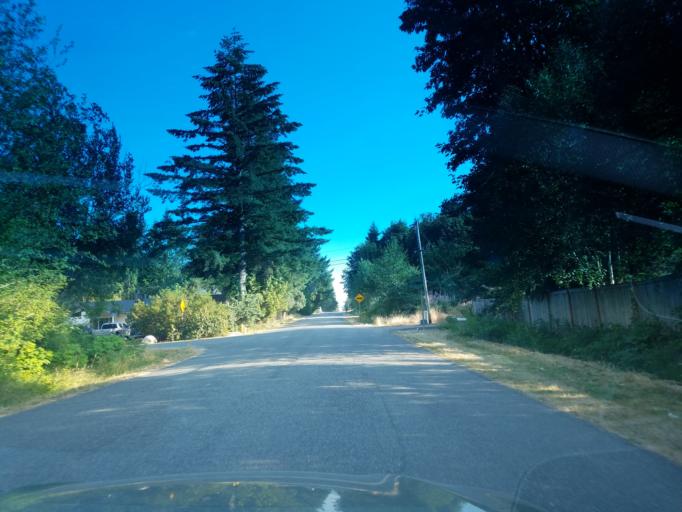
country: US
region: Washington
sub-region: King County
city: Ames Lake
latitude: 47.6536
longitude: -121.9869
